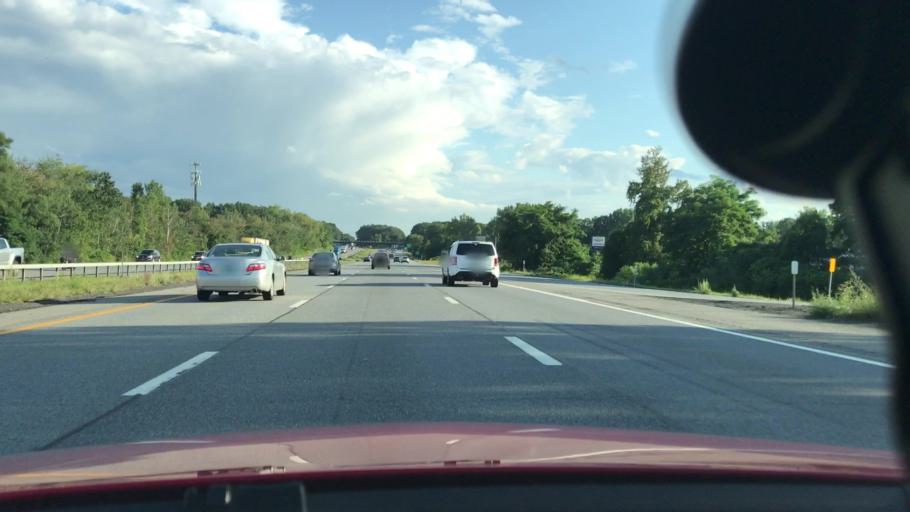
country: US
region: New York
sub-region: Saratoga County
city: Country Knolls
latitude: 42.8601
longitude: -73.7751
